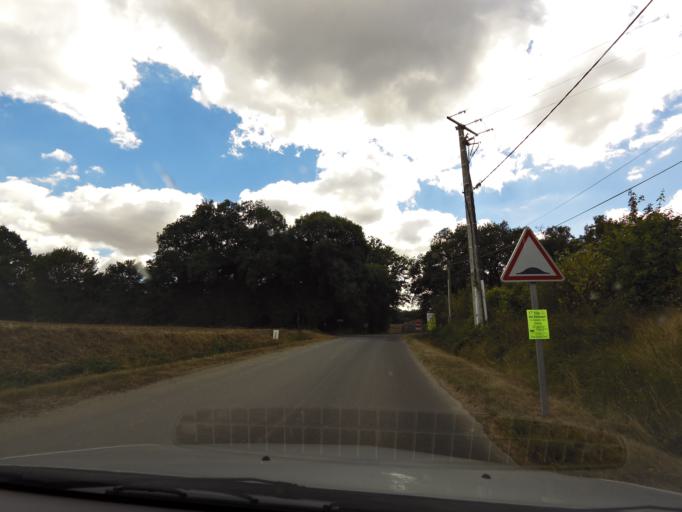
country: FR
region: Poitou-Charentes
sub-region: Departement des Deux-Sevres
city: Beauvoir-sur-Niort
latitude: 46.1449
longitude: -0.3947
